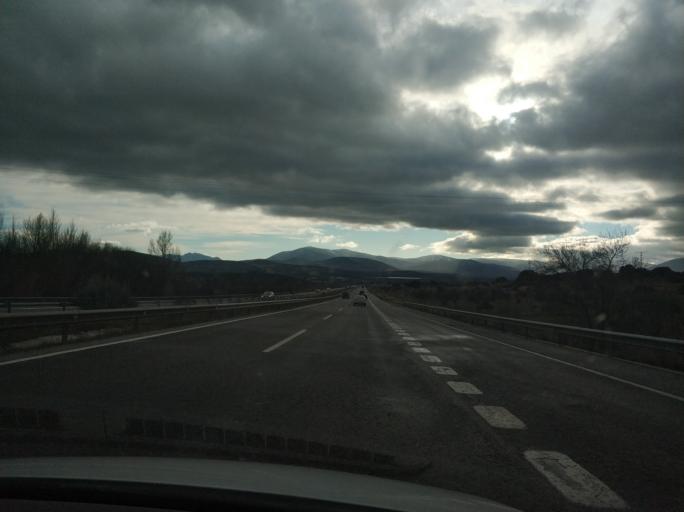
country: ES
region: Madrid
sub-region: Provincia de Madrid
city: Gascones
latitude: 41.0248
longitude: -3.6242
